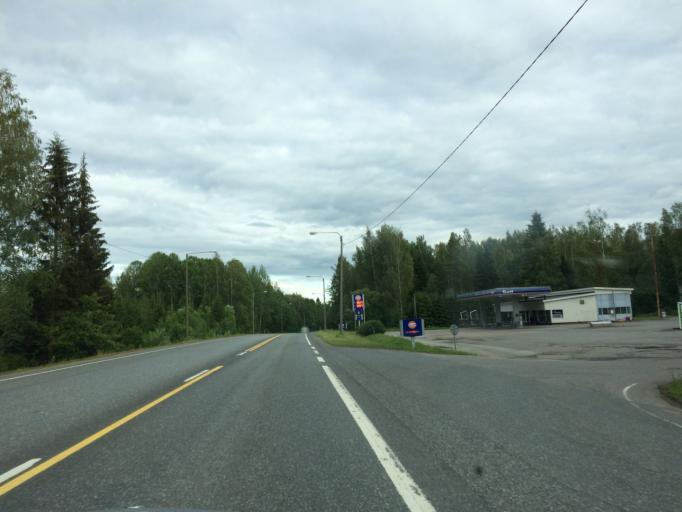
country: FI
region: Haeme
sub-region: Haemeenlinna
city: Haemeenlinna
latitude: 60.9490
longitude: 24.5085
